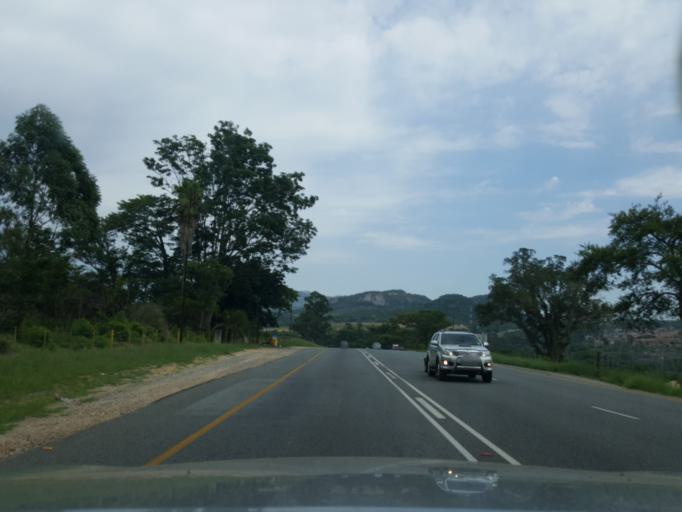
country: ZA
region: Mpumalanga
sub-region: Ehlanzeni District
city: Nelspruit
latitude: -25.4775
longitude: 31.1065
